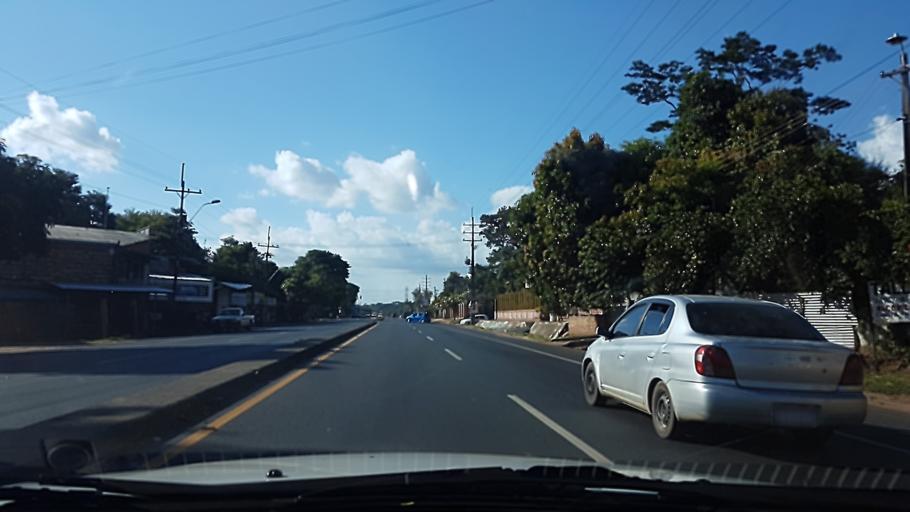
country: PY
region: Central
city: San Antonio
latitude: -25.4304
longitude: -57.5371
